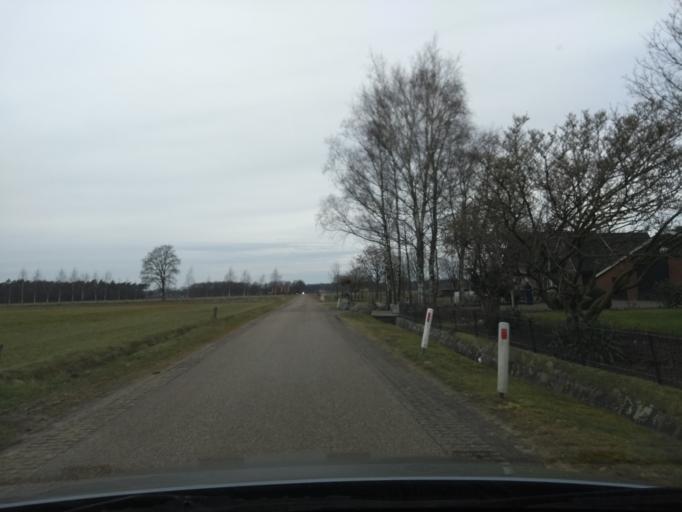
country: NL
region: Overijssel
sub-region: Gemeente Borne
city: Borne
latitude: 52.3531
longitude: 6.7353
